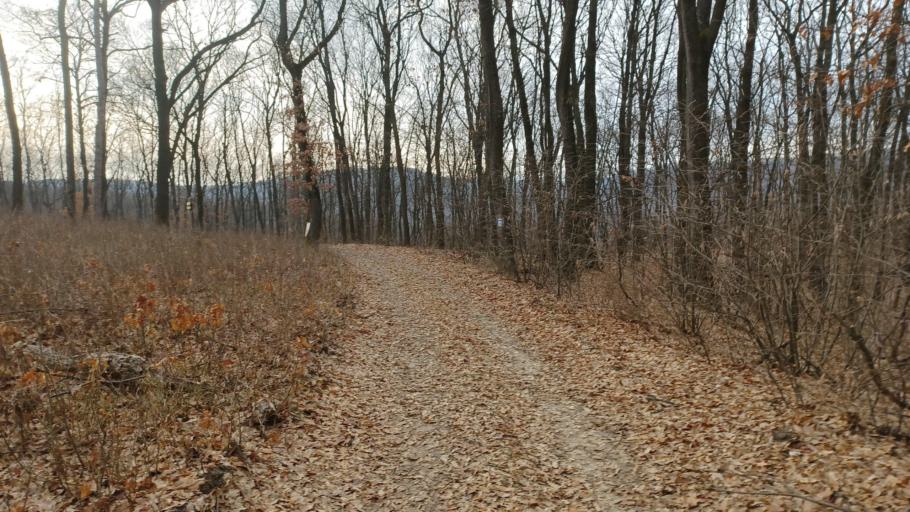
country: HU
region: Tolna
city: Szentgalpuszta
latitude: 46.3353
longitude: 18.6249
